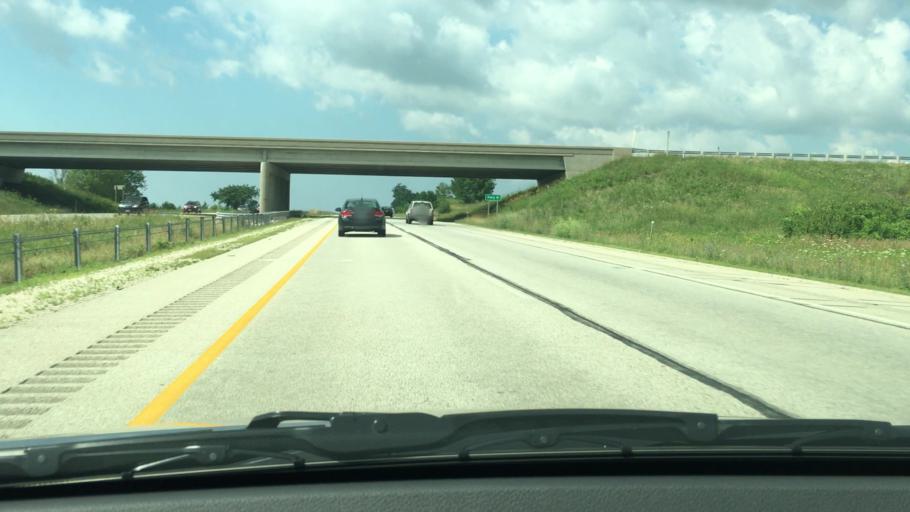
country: US
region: Wisconsin
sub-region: Fond du Lac County
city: Fond du Lac
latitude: 43.6889
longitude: -88.4417
